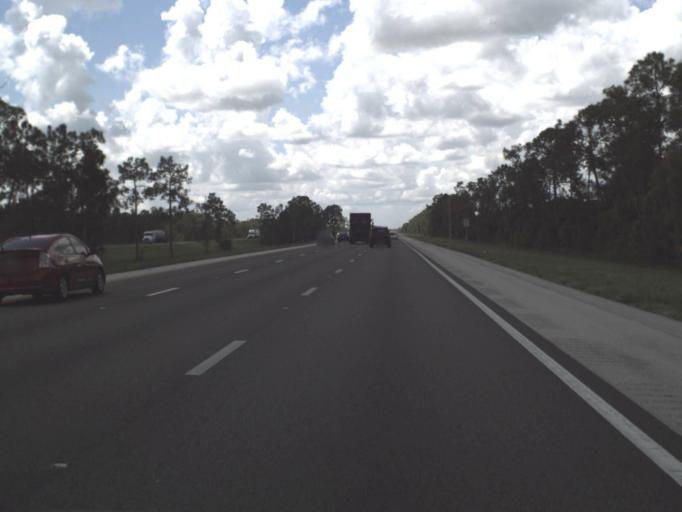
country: US
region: Florida
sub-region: Lee County
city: Estero
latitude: 26.4072
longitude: -81.7734
